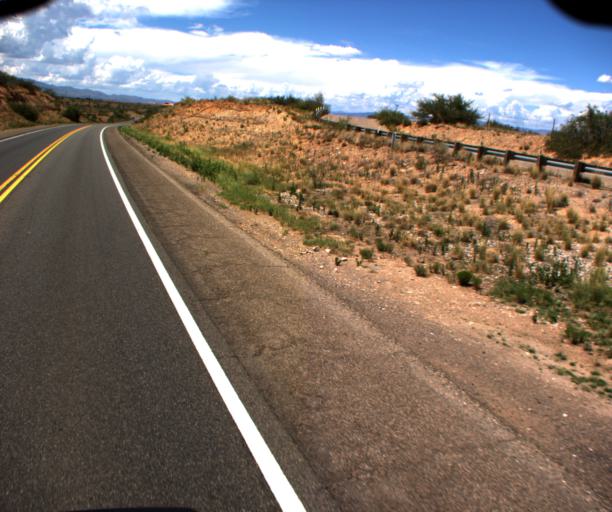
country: US
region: Arizona
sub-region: Yavapai County
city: Camp Verde
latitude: 34.6032
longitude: -111.9065
